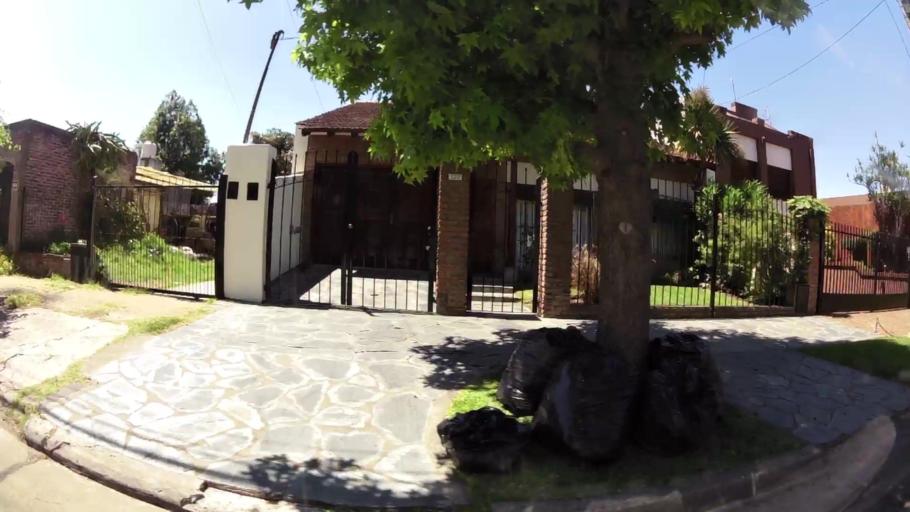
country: AR
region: Buenos Aires
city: Ituzaingo
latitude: -34.6732
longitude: -58.6878
